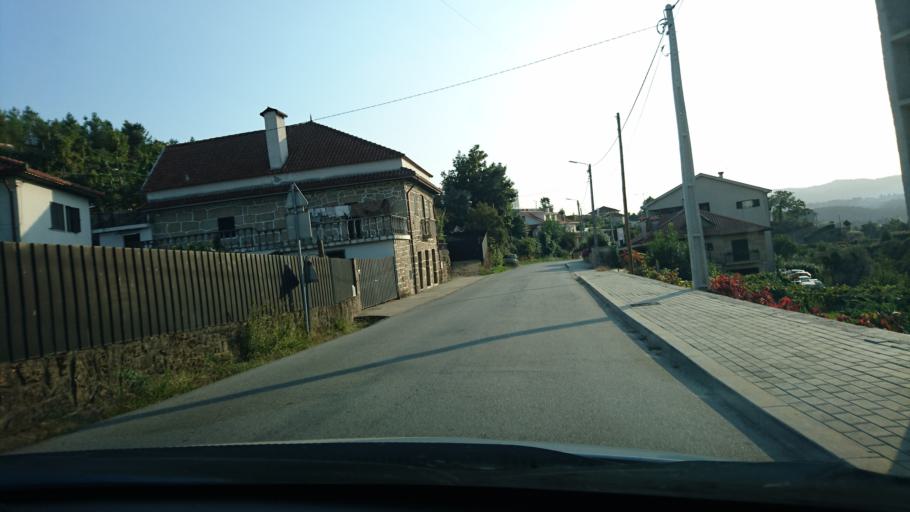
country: PT
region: Vila Real
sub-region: Mondim de Basto
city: Mondim de Basto
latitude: 41.4176
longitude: -7.9440
